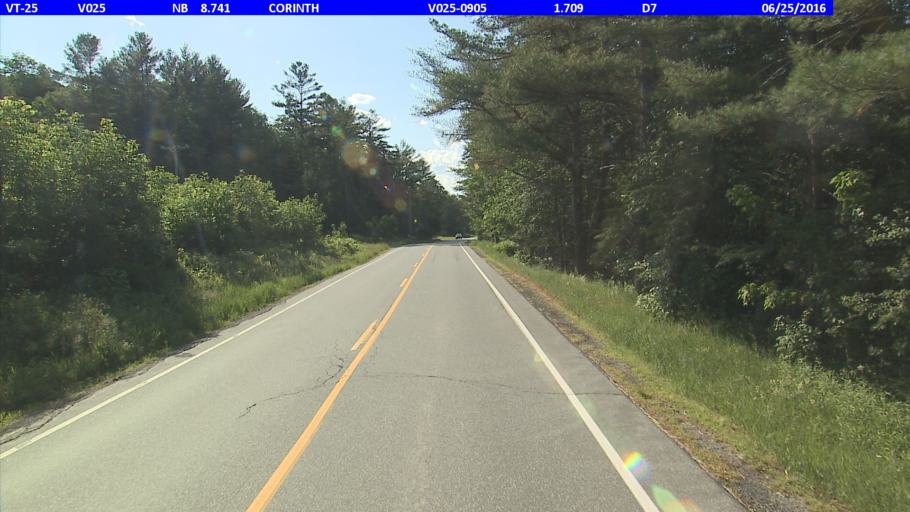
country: US
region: New Hampshire
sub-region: Grafton County
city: Haverhill
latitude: 44.0569
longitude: -72.2278
